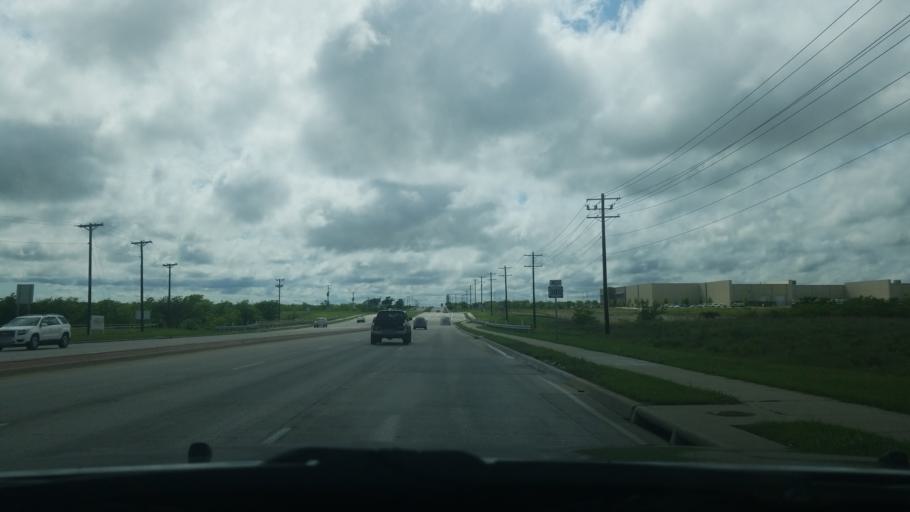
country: US
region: Texas
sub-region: Denton County
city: Krum
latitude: 33.2308
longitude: -97.1975
